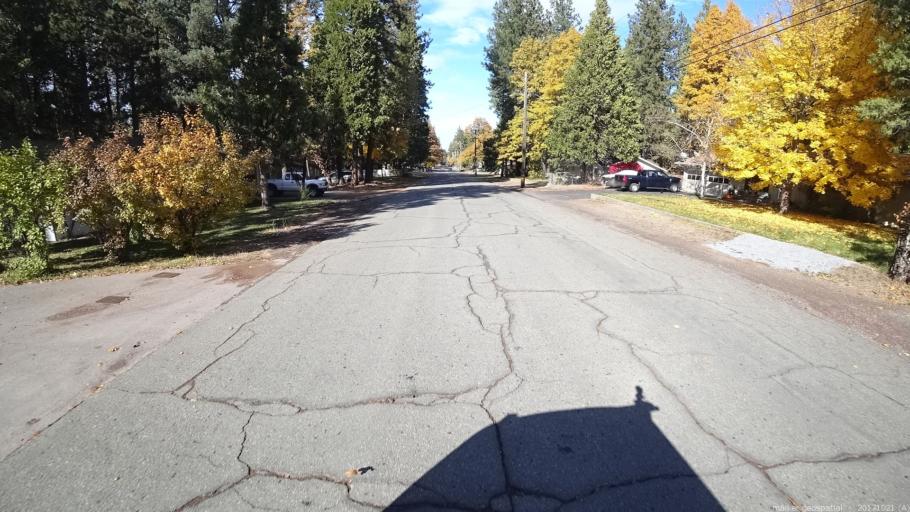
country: US
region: California
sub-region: Shasta County
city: Burney
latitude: 40.8759
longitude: -121.6575
